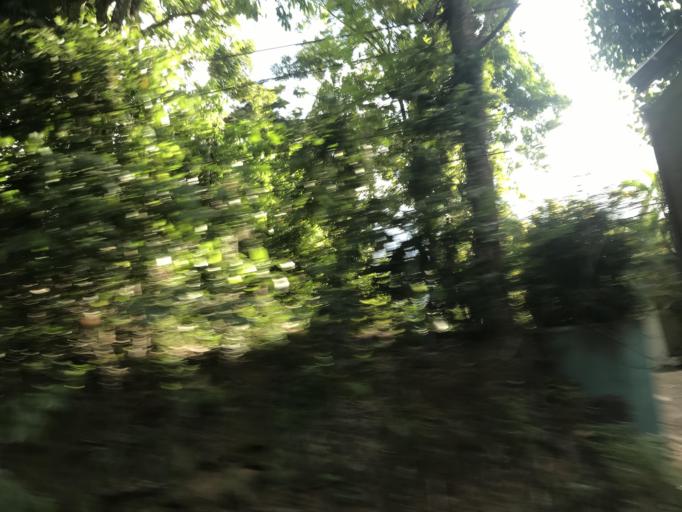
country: LK
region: Western
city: Gampaha
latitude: 7.0651
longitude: 80.0068
